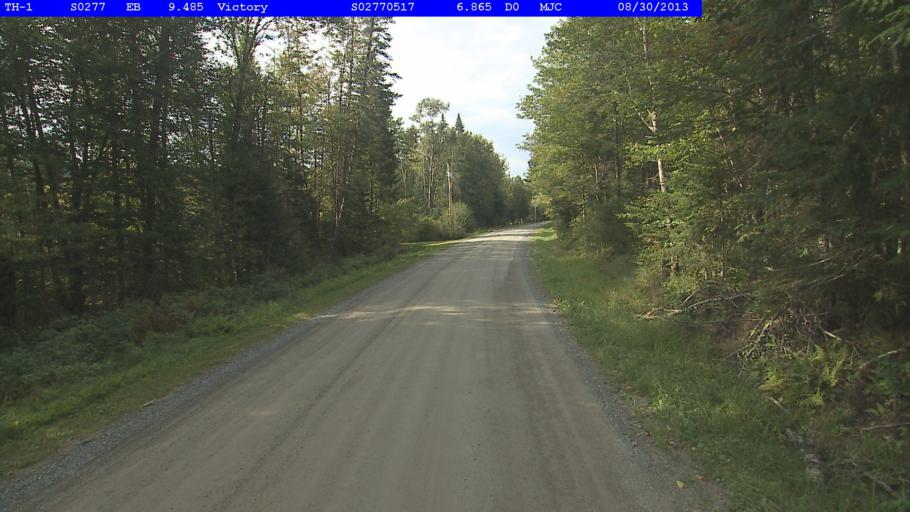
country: US
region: Vermont
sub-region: Caledonia County
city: Lyndonville
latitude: 44.5668
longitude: -71.7892
